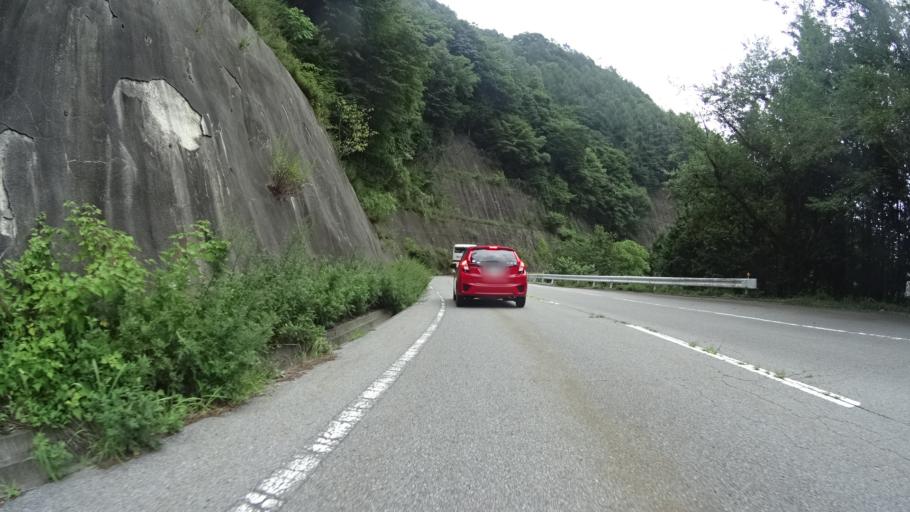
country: JP
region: Yamanashi
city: Enzan
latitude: 35.7987
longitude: 138.6749
